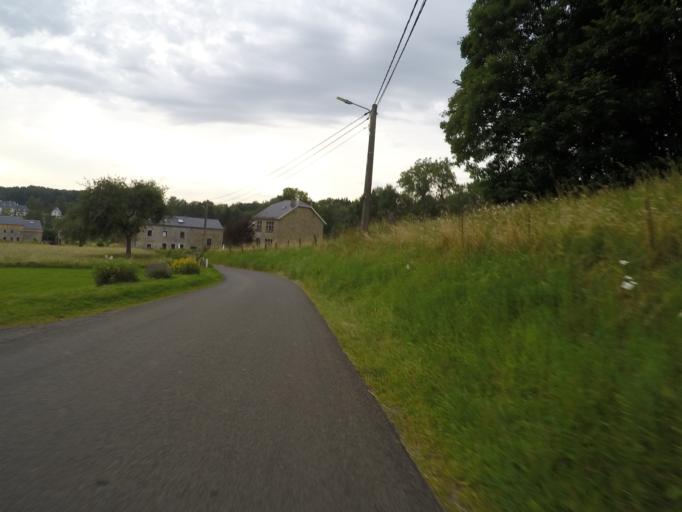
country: BE
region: Wallonia
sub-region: Province de Namur
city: Assesse
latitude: 50.3239
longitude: 5.0394
